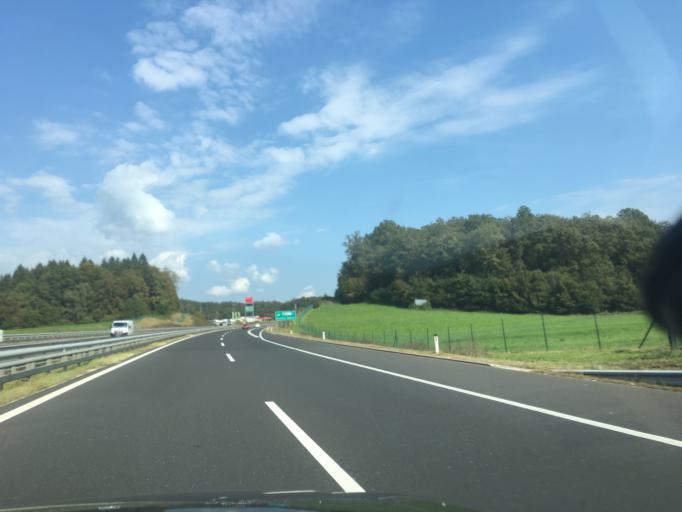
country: SI
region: Novo Mesto
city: Novo Mesto
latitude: 45.8383
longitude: 15.2116
